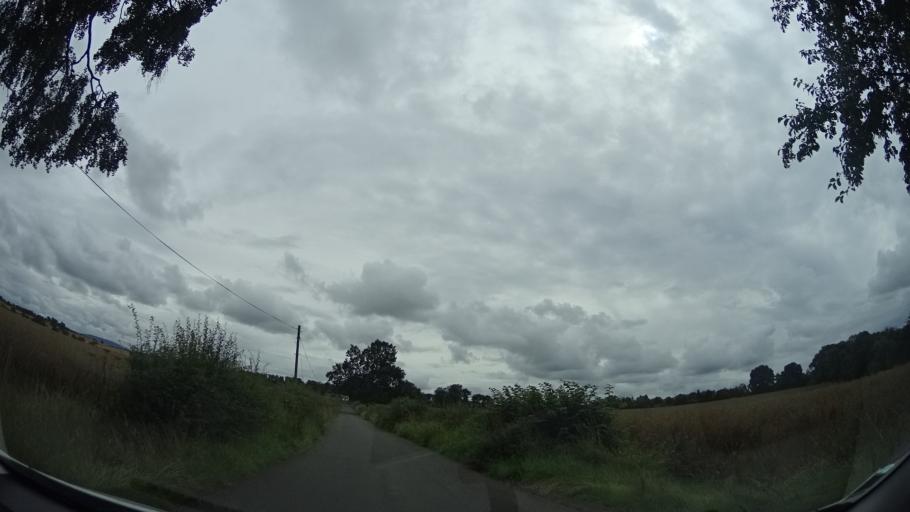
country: GB
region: Scotland
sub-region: West Lothian
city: Kirknewton
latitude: 55.9158
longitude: -3.4311
